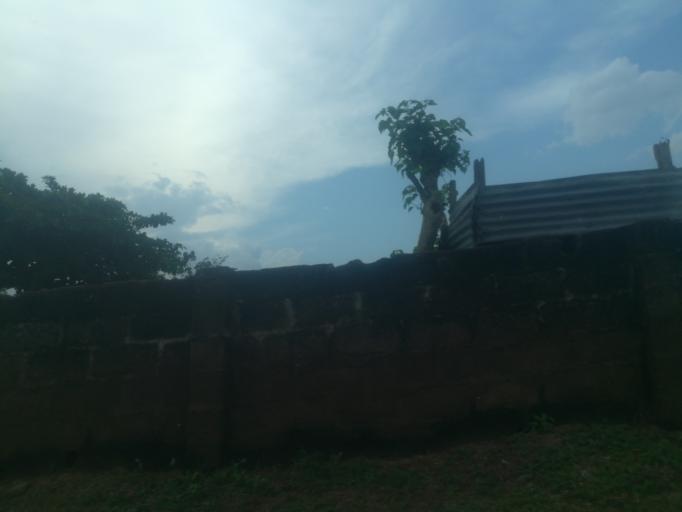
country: NG
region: Oyo
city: Ibadan
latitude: 7.3658
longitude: 3.8478
